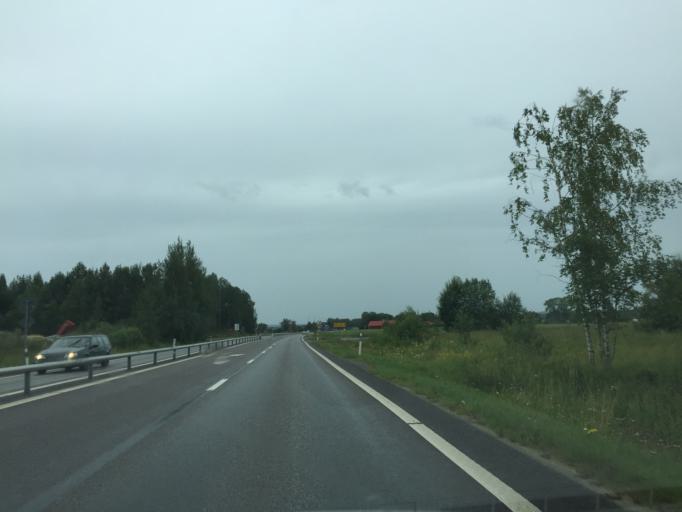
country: SE
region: OErebro
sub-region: Orebro Kommun
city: Orebro
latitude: 59.2019
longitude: 15.2424
